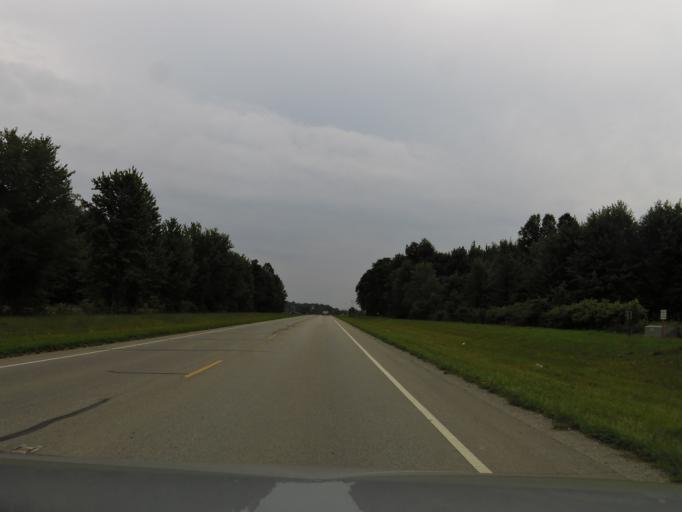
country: US
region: Ohio
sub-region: Brown County
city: Georgetown
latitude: 38.8936
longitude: -83.8981
